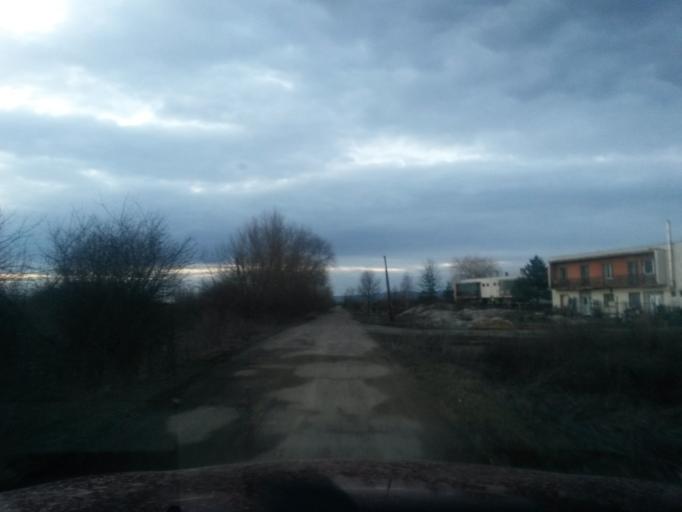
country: SK
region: Kosicky
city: Sobrance
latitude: 48.6880
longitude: 22.0537
